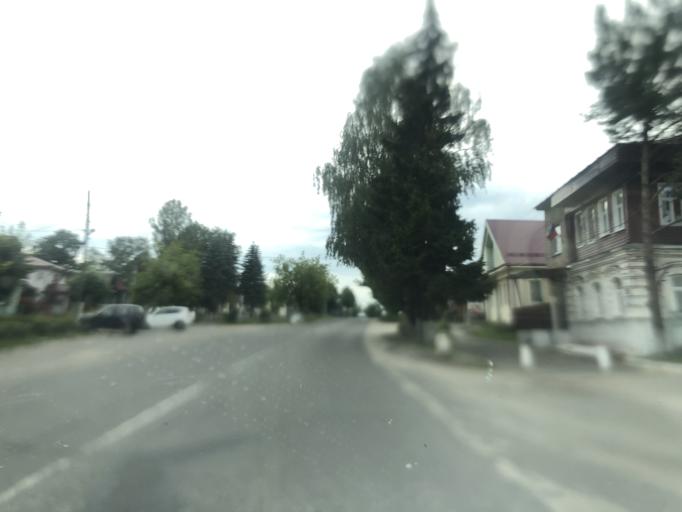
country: RU
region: Ivanovo
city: Pestyaki
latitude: 56.7081
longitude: 42.6694
